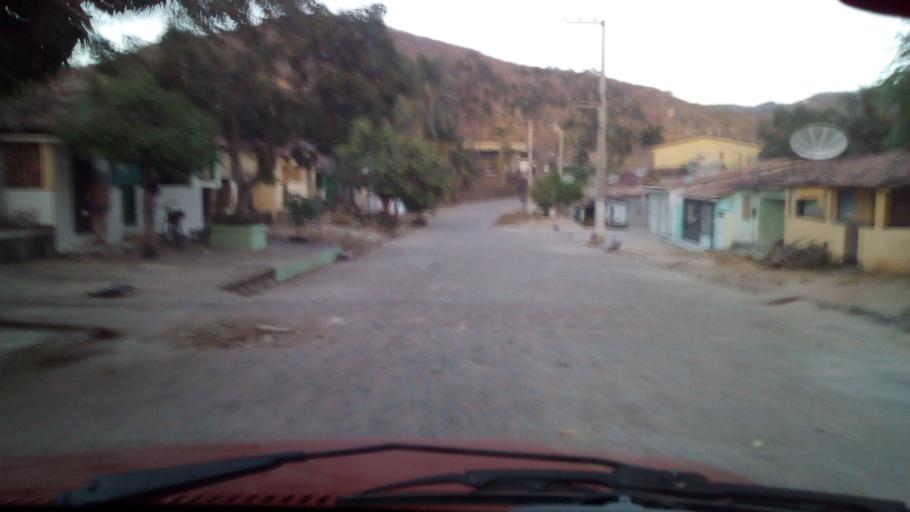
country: BR
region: Paraiba
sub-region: Belem
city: Belem
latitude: -6.7207
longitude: -35.5396
